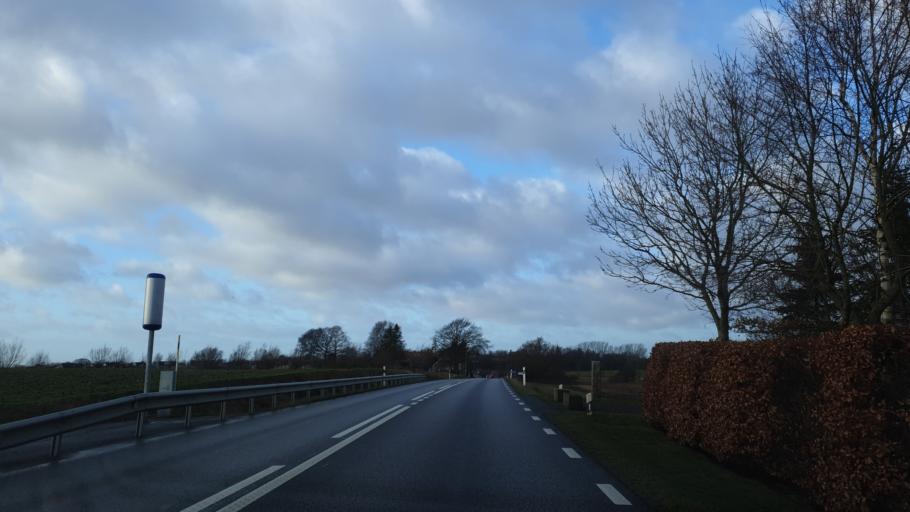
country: SE
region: Skane
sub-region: Malmo
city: Oxie
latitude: 55.4622
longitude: 13.1492
